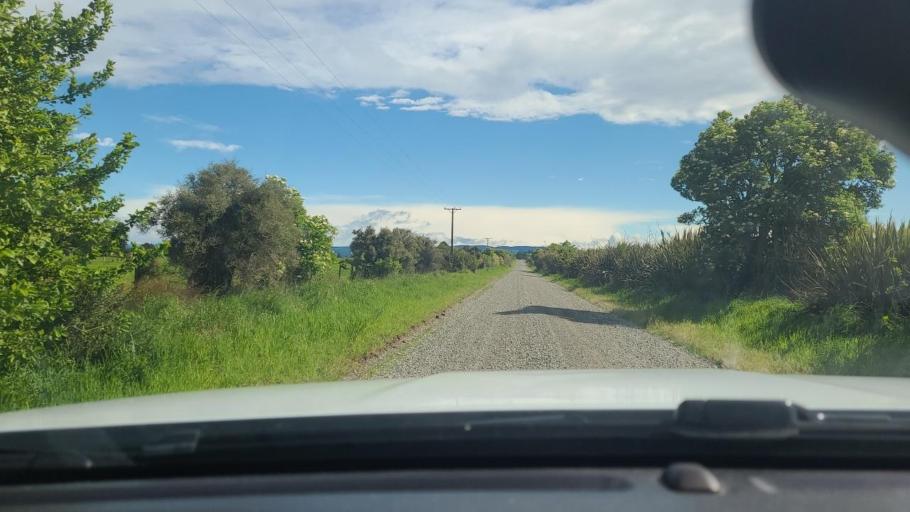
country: NZ
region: Southland
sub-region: Southland District
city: Winton
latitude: -46.0985
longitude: 168.2583
